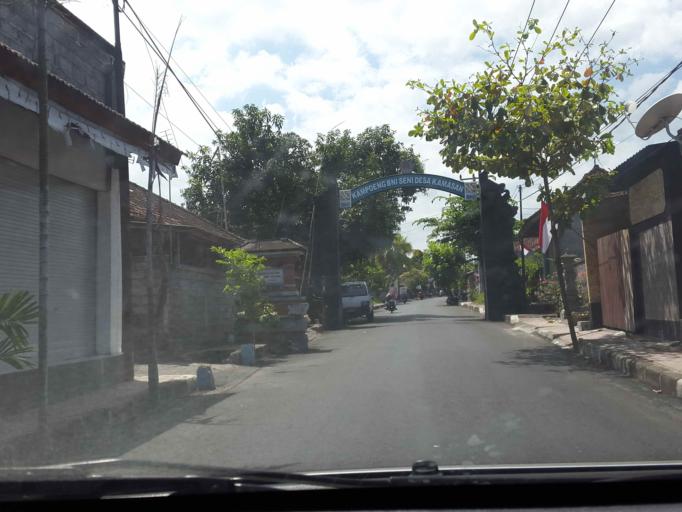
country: ID
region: Bali
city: Semarapura
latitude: -8.5534
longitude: 115.4072
